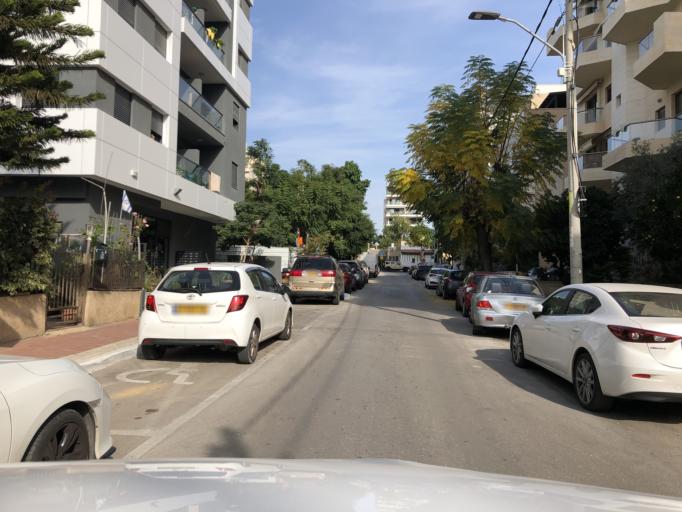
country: IL
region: Tel Aviv
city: Bene Beraq
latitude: 32.0714
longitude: 34.8263
